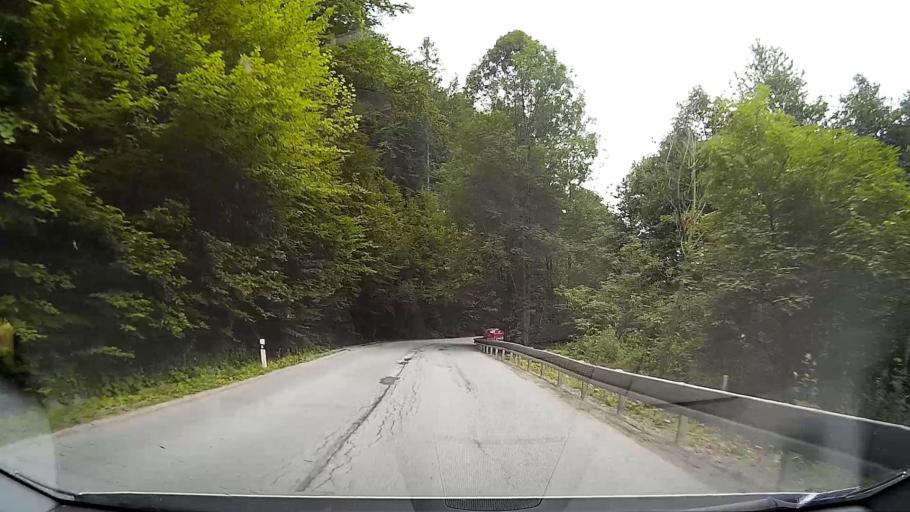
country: SK
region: Banskobystricky
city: Tisovec
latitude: 48.7079
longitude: 19.9931
